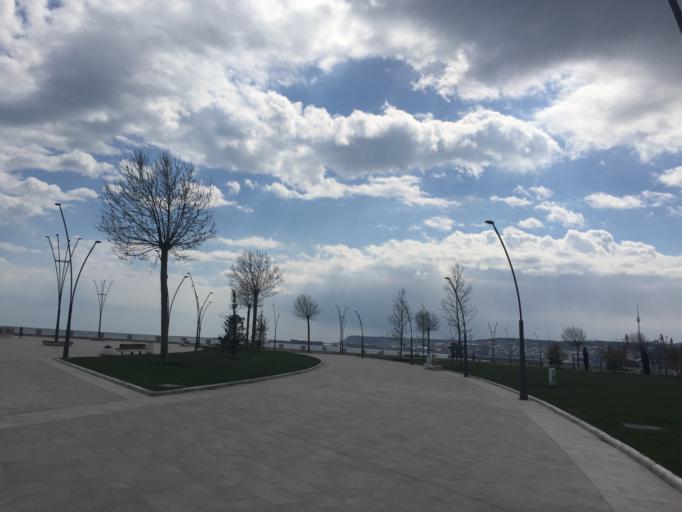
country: AZ
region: Baki
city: Baku
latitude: 40.3747
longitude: 49.8714
